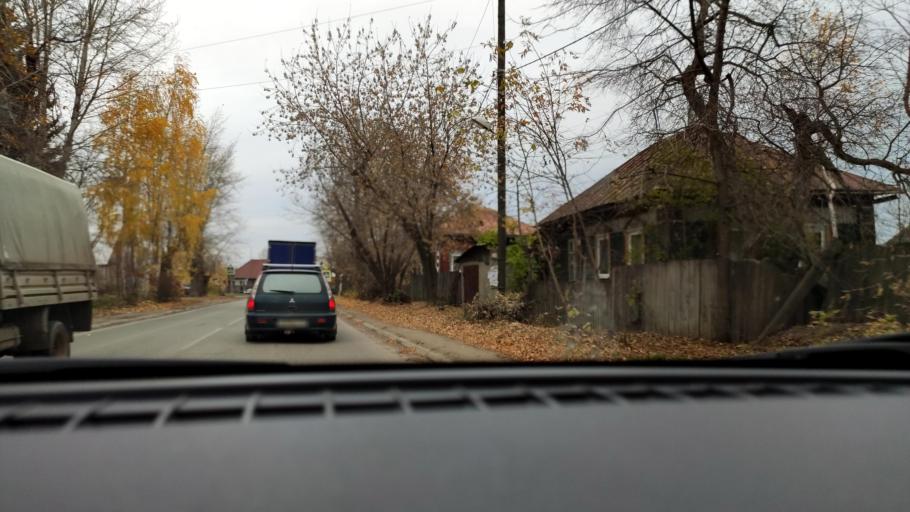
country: RU
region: Perm
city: Perm
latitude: 58.0169
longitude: 56.3148
